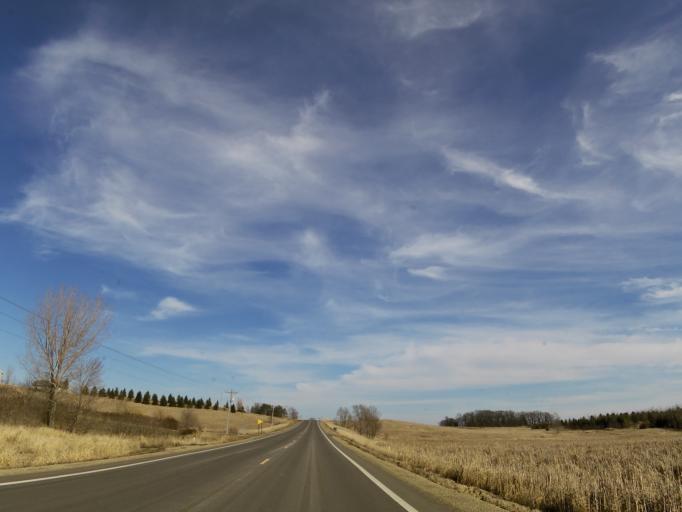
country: US
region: Minnesota
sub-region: Scott County
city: Elko New Market
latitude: 44.5440
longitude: -93.3322
